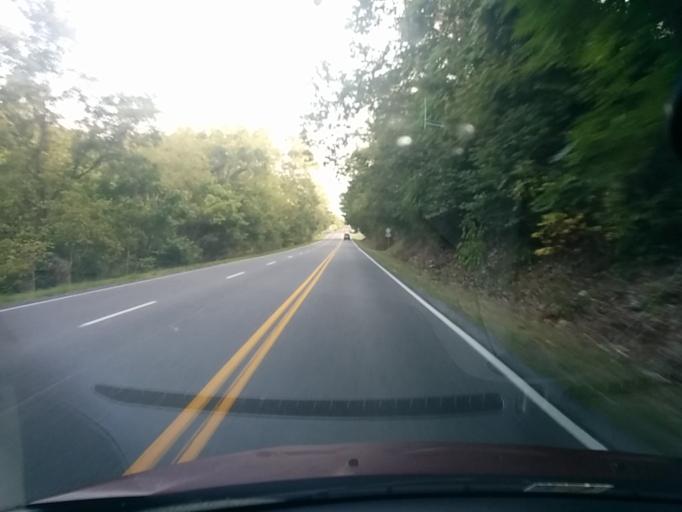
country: US
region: Virginia
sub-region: City of Lexington
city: Lexington
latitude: 37.7650
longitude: -79.4468
